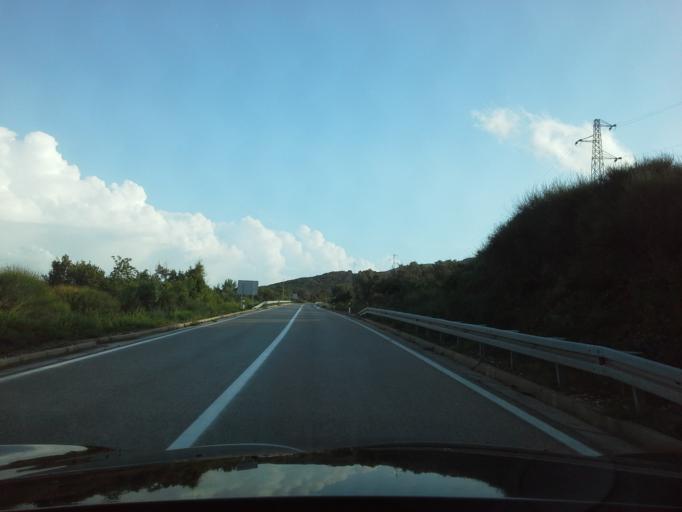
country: HR
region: Primorsko-Goranska
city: Mali Losinj
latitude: 44.6608
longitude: 14.3899
